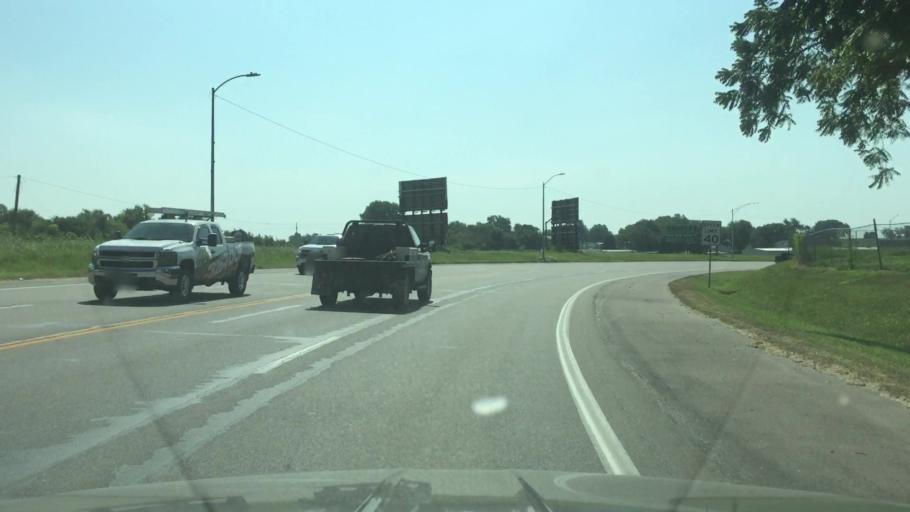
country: US
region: Missouri
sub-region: Pettis County
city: Sedalia
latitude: 38.7029
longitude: -93.1943
